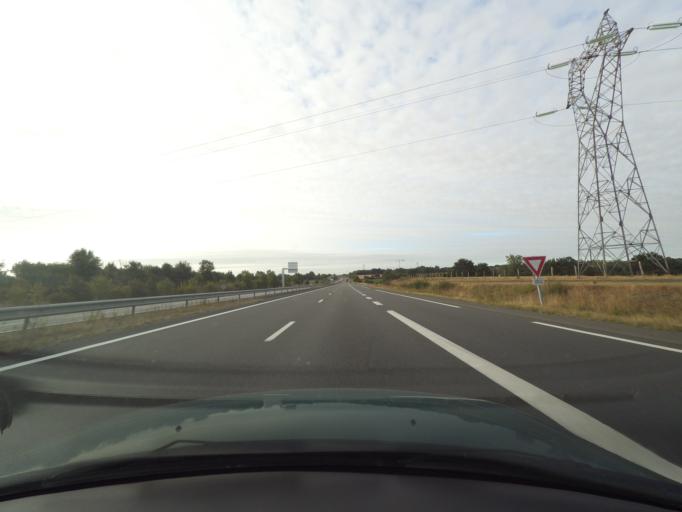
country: FR
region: Pays de la Loire
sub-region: Departement de Maine-et-Loire
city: La Seguiniere
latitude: 47.0583
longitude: -0.9232
